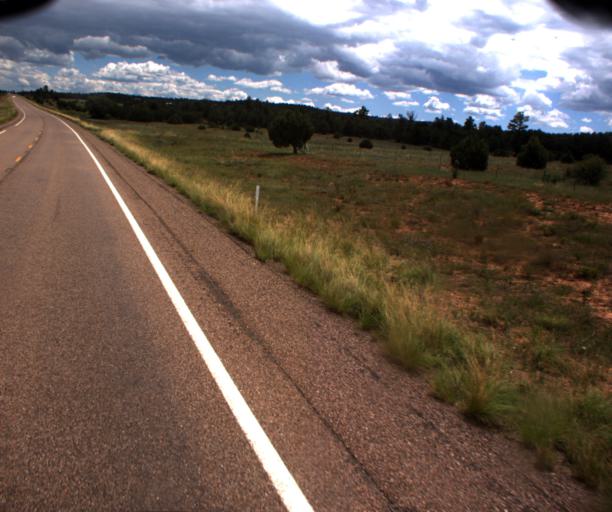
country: US
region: Arizona
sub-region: Navajo County
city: Linden
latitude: 34.3488
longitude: -110.3063
